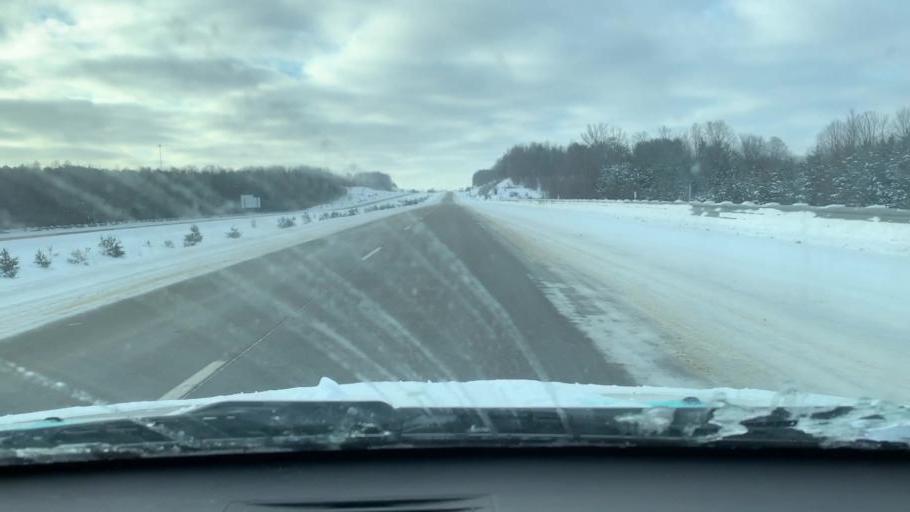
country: US
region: Michigan
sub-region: Wexford County
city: Manton
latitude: 44.4021
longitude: -85.3818
